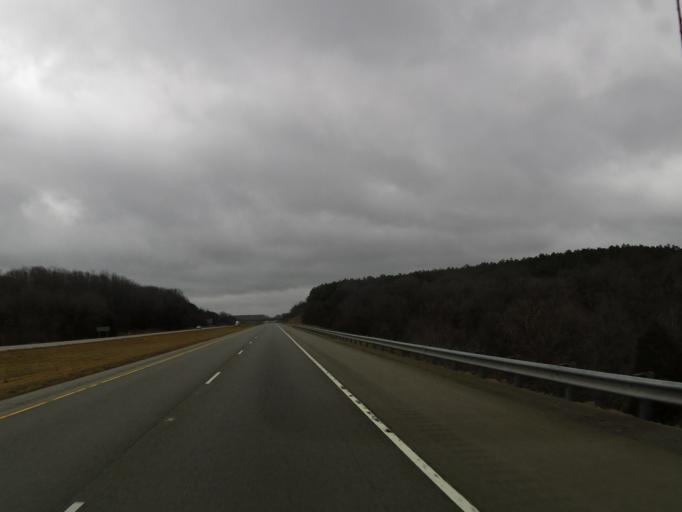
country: US
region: Illinois
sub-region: Johnson County
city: Goreville
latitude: 37.5208
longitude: -88.9143
